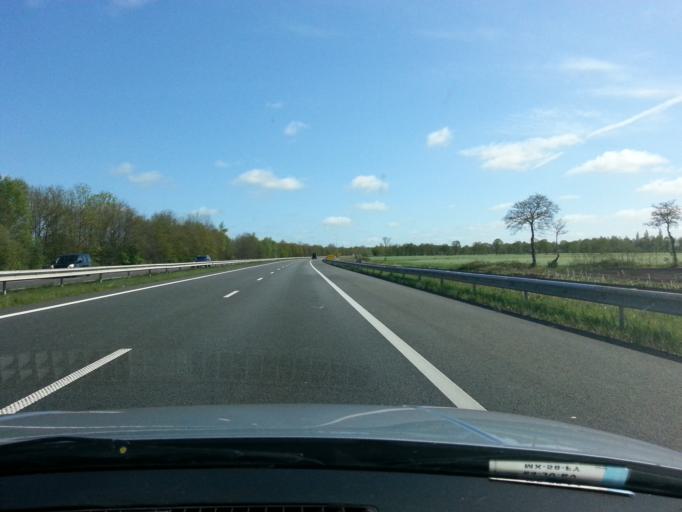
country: NL
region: Friesland
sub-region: Gemeente Smallingerland
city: Drachtstercompagnie
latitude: 53.1181
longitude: 6.1591
